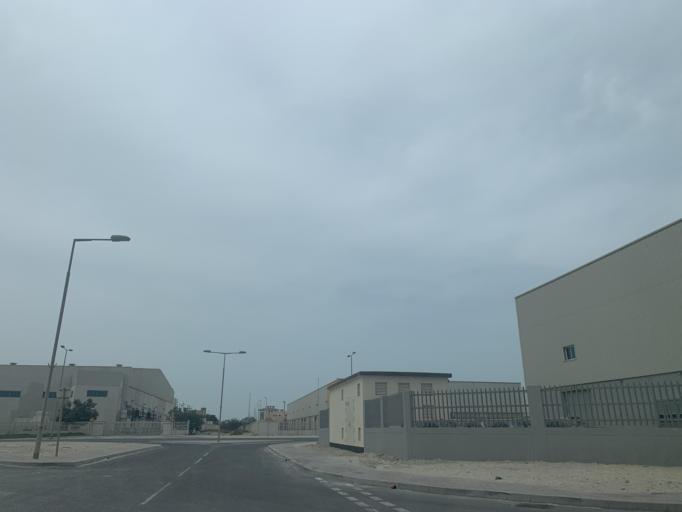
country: BH
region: Muharraq
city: Al Hadd
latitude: 26.2142
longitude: 50.6741
